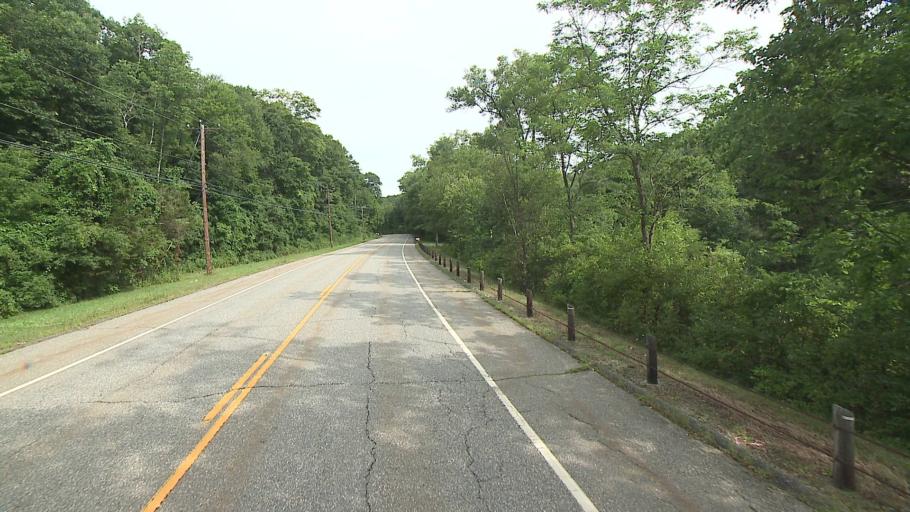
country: US
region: Connecticut
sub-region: Litchfield County
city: New Preston
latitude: 41.6728
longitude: -73.3246
